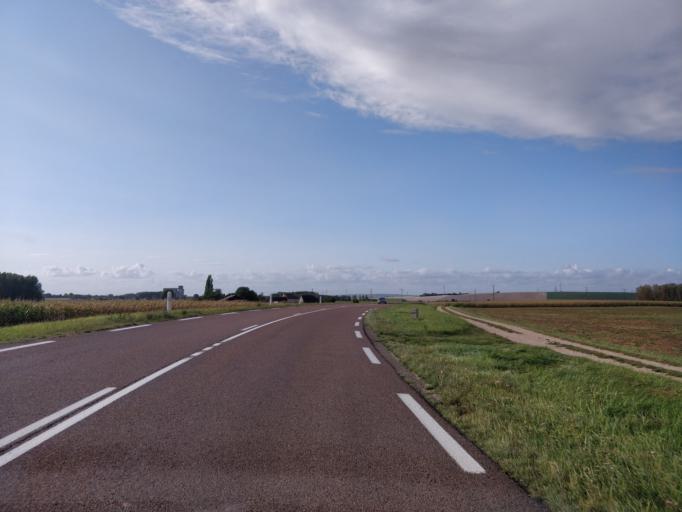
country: FR
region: Champagne-Ardenne
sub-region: Departement de l'Aube
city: Verrieres
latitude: 48.2768
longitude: 4.1987
